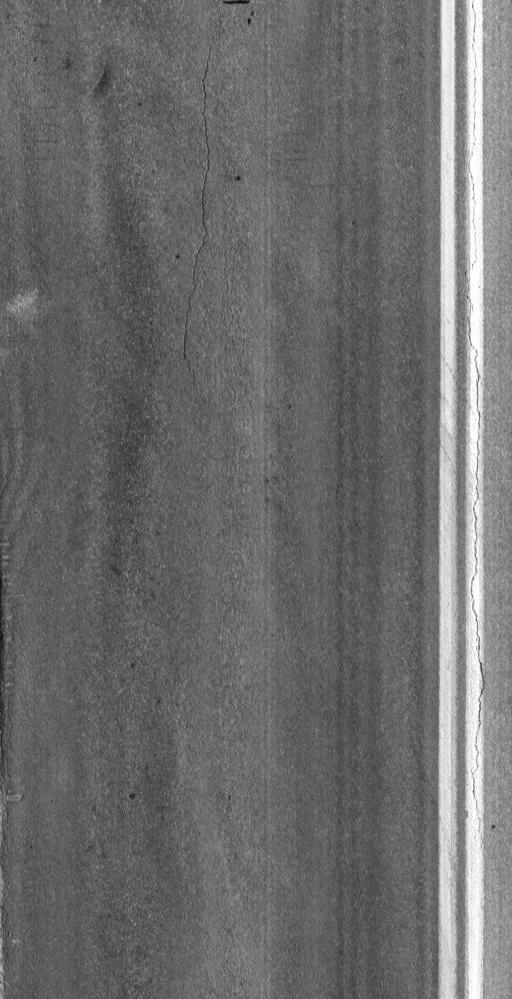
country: US
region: Vermont
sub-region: Chittenden County
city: Hinesburg
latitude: 44.3573
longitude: -73.2213
